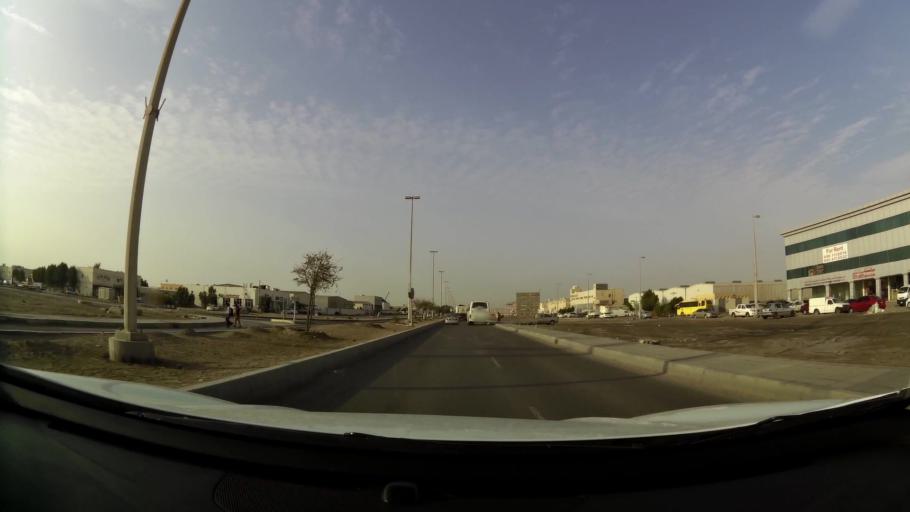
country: AE
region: Abu Dhabi
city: Abu Dhabi
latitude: 24.3506
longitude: 54.5171
